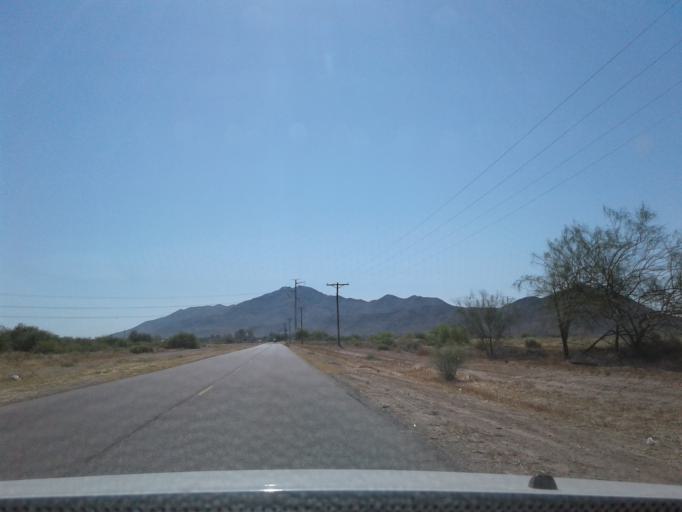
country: US
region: Arizona
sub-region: Maricopa County
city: Laveen
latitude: 33.3339
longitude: -112.1819
